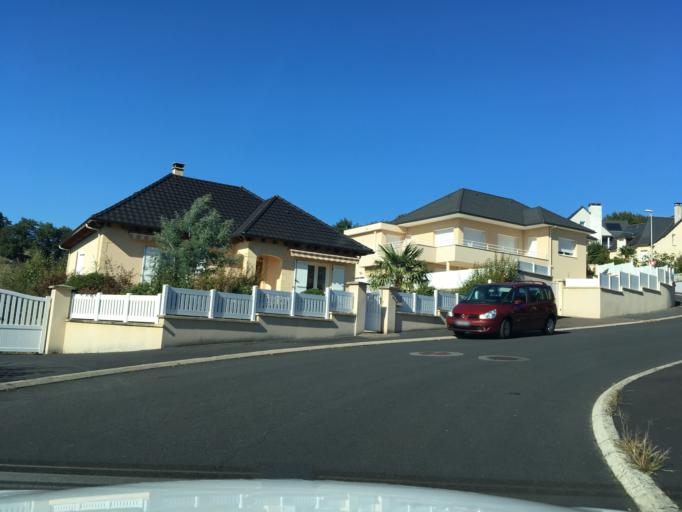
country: FR
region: Limousin
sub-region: Departement de la Correze
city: Malemort-sur-Correze
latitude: 45.1697
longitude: 1.5459
